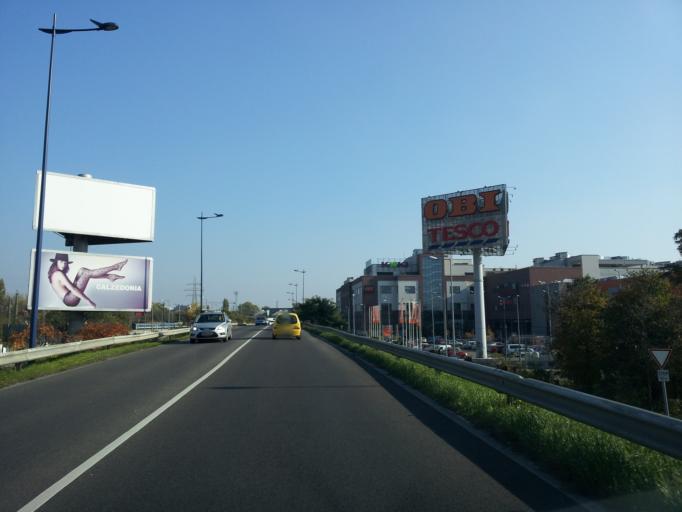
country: HU
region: Budapest
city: Budapest XIX. keruelet
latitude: 47.4641
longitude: 19.1429
